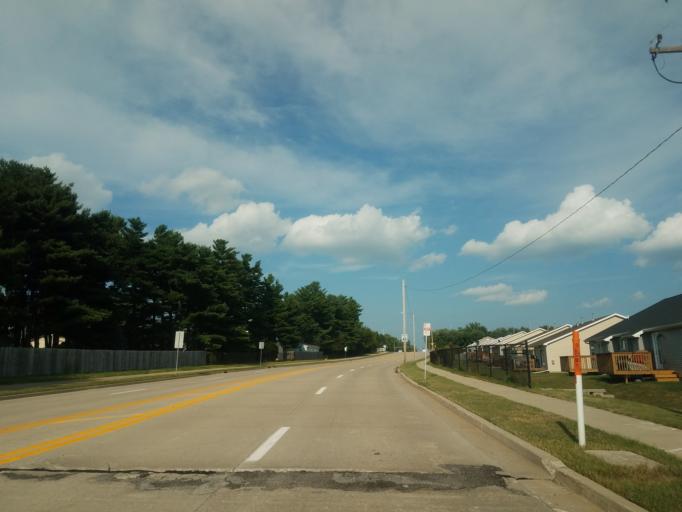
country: US
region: Illinois
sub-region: McLean County
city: Bloomington
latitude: 40.4496
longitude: -89.0106
